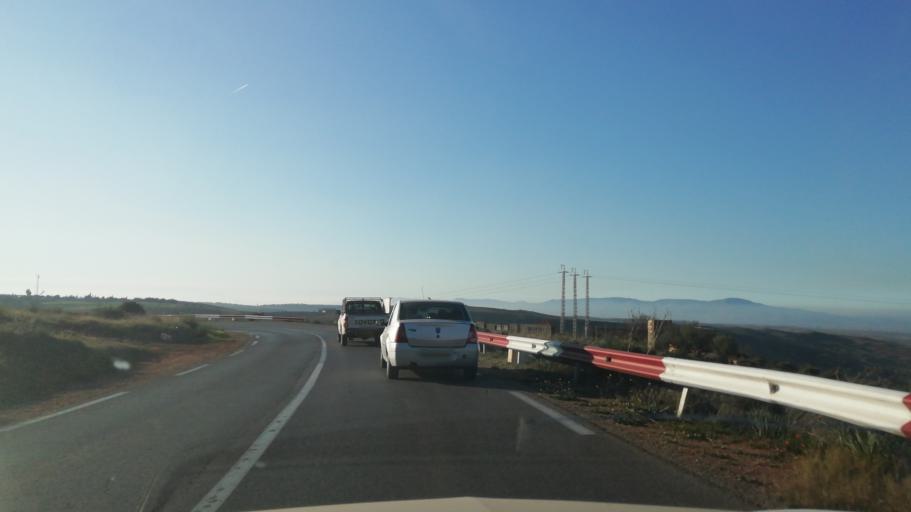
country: DZ
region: Tlemcen
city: Beni Mester
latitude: 34.8493
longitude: -1.4621
